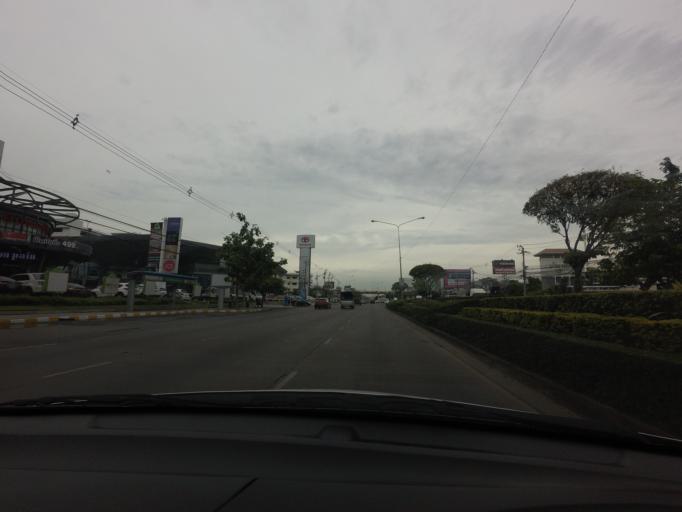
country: TH
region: Bangkok
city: Bueng Kum
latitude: 13.7737
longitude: 100.6674
